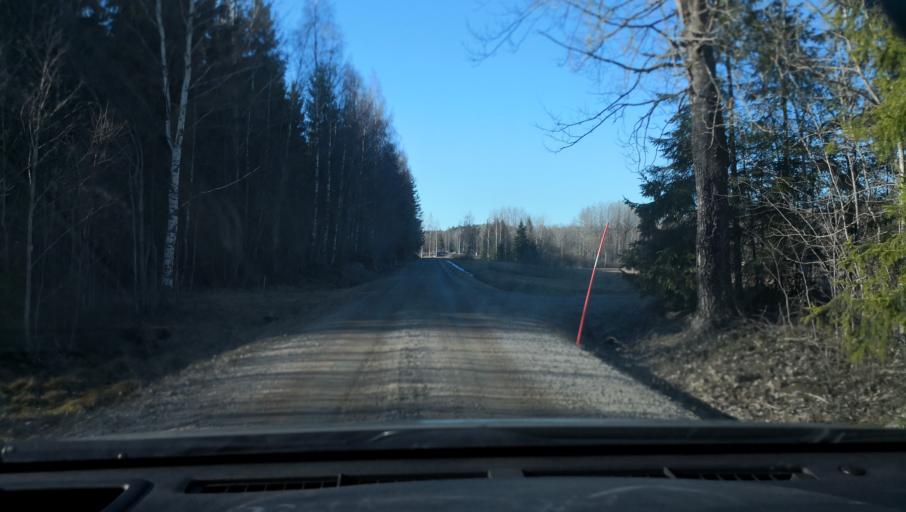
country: SE
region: Dalarna
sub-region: Avesta Kommun
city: Horndal
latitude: 60.1792
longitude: 16.6284
